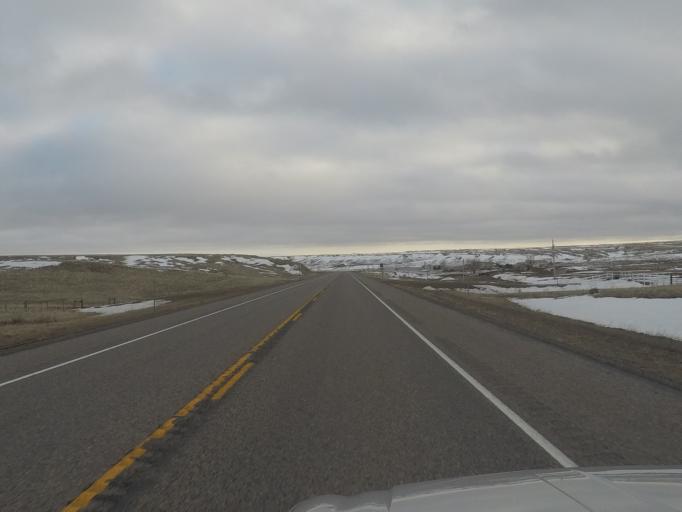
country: US
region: Montana
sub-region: Yellowstone County
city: Billings
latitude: 45.8837
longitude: -108.6702
